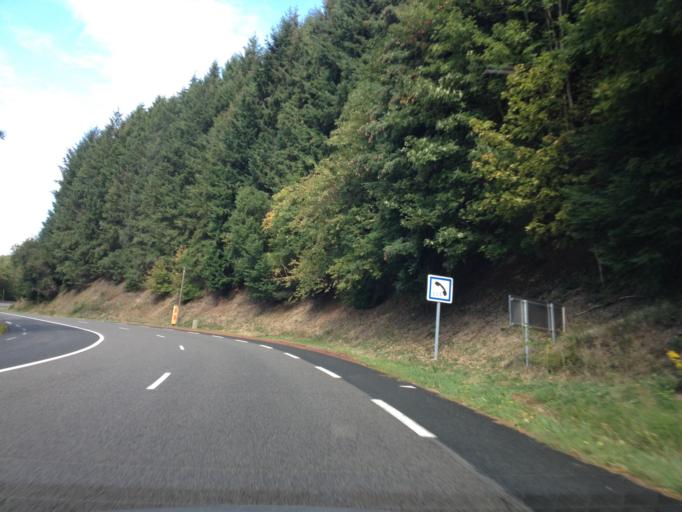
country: FR
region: Rhone-Alpes
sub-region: Departement de la Loire
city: Violay
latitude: 45.8948
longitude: 4.3664
